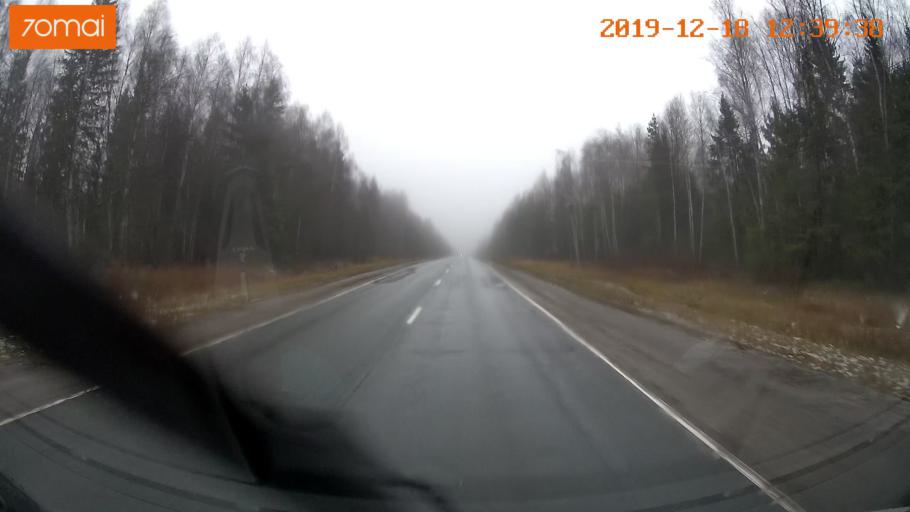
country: RU
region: Moskovskaya
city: Vysokovsk
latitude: 56.1675
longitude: 36.6126
